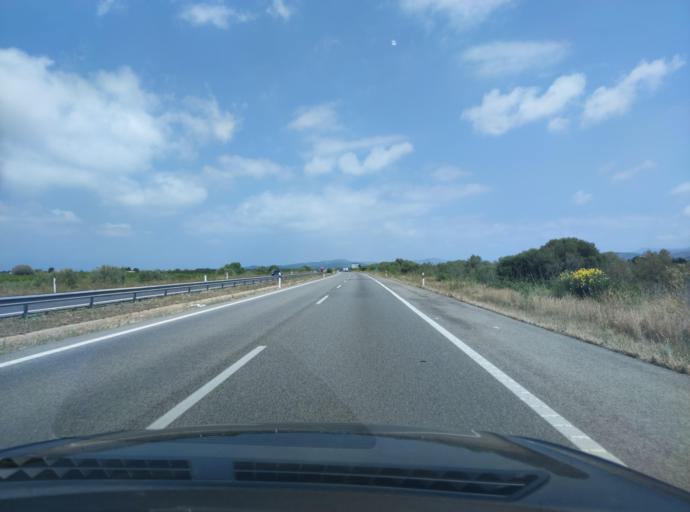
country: ES
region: Catalonia
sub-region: Provincia de Tarragona
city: Alcanar
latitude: 40.5280
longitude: 0.4181
